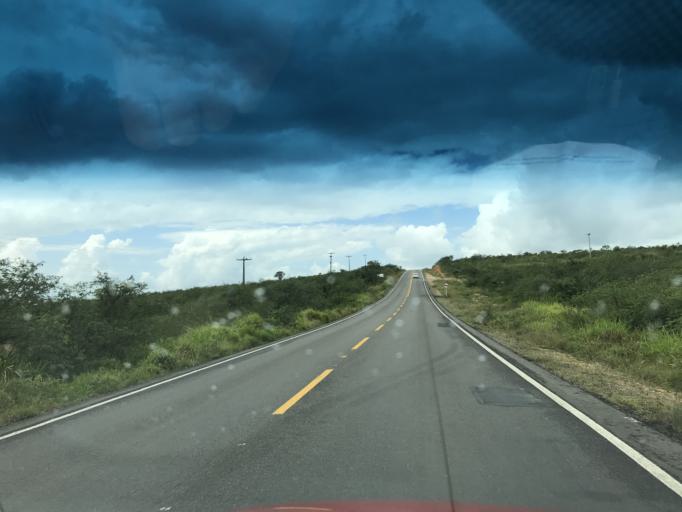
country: BR
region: Bahia
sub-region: Conceicao Do Almeida
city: Conceicao do Almeida
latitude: -12.6744
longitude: -39.2668
